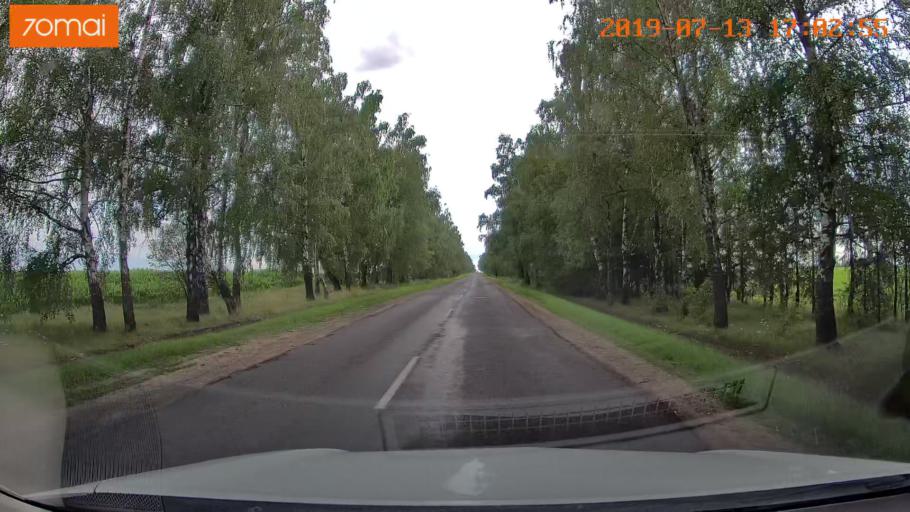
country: BY
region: Mogilev
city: Kirawsk
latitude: 53.2812
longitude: 29.3823
